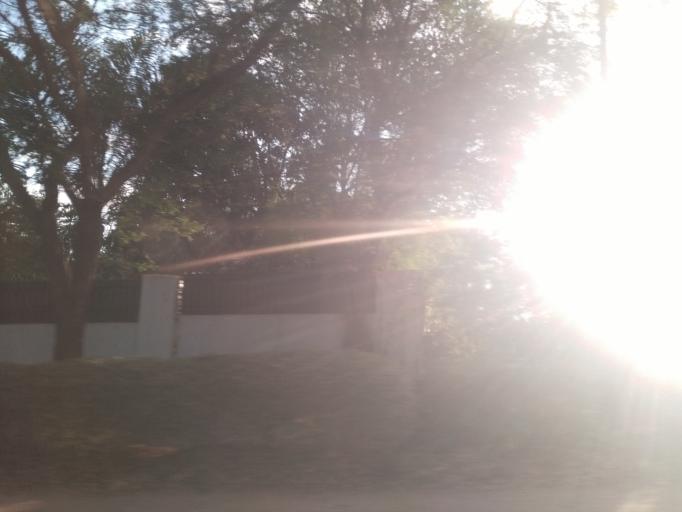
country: TZ
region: Dar es Salaam
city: Magomeni
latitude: -6.7847
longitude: 39.2709
